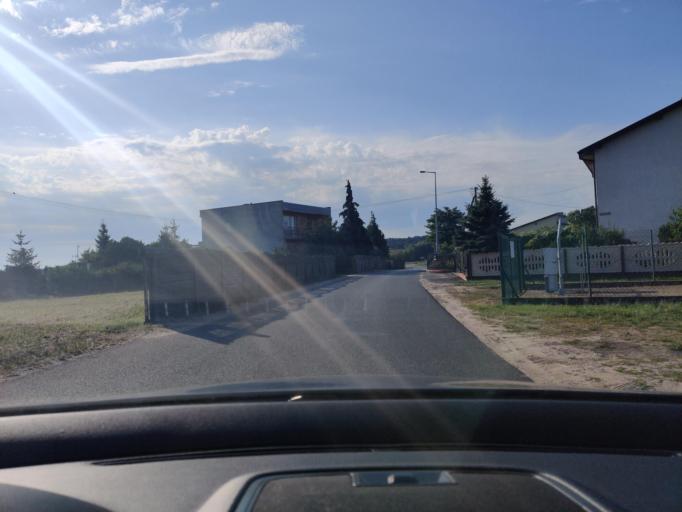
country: PL
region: Greater Poland Voivodeship
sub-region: Konin
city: Konin
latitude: 52.1887
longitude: 18.3223
